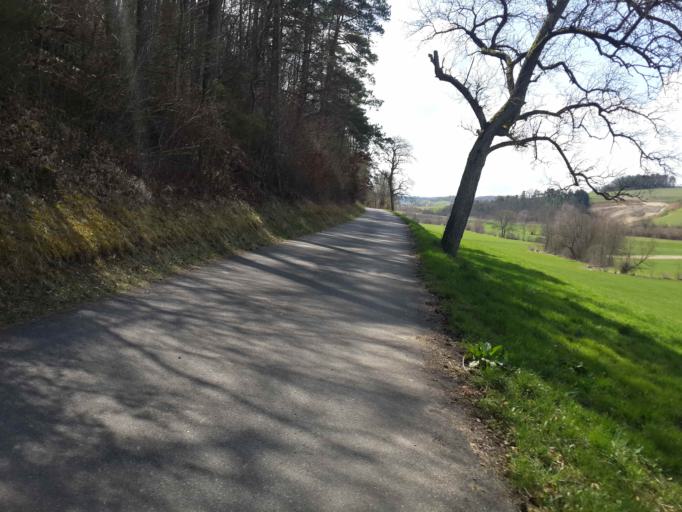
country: DE
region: Baden-Wuerttemberg
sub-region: Regierungsbezirk Stuttgart
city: Bad Mergentheim
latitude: 49.4600
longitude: 9.7719
